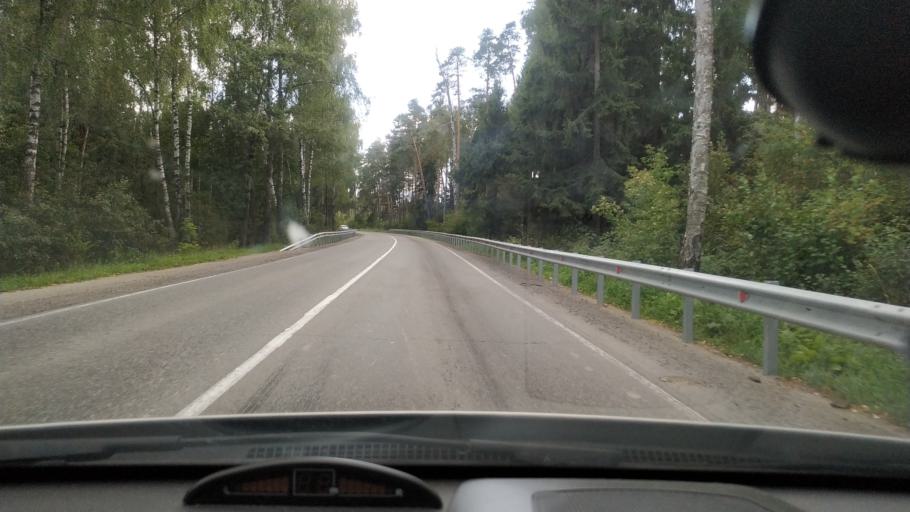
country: RU
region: Moskovskaya
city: Zheleznodorozhnyy
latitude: 55.7905
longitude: 38.0362
